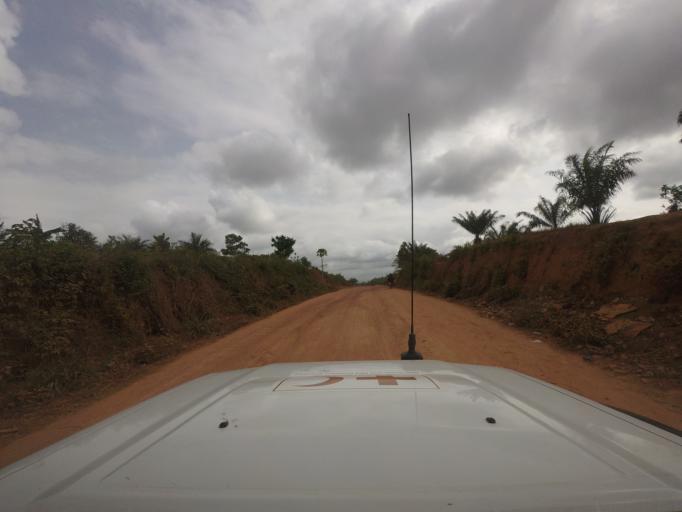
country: LR
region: Bong
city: Gbarnga
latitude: 7.0158
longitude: -9.4751
